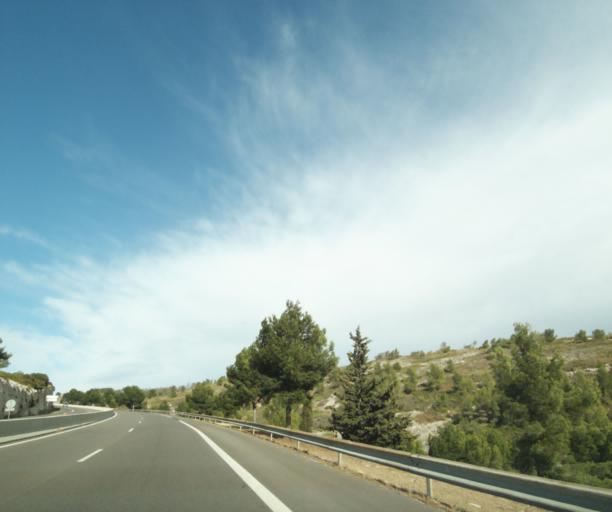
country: FR
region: Provence-Alpes-Cote d'Azur
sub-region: Departement des Bouches-du-Rhone
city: Carry-le-Rouet
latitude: 43.3430
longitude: 5.1695
